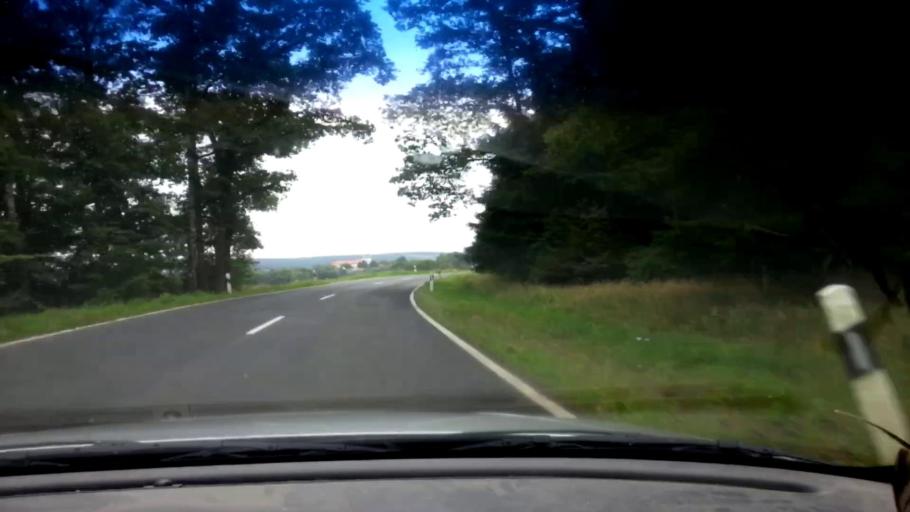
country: DE
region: Bavaria
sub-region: Upper Palatinate
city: Waldsassen
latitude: 50.0160
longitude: 12.3114
